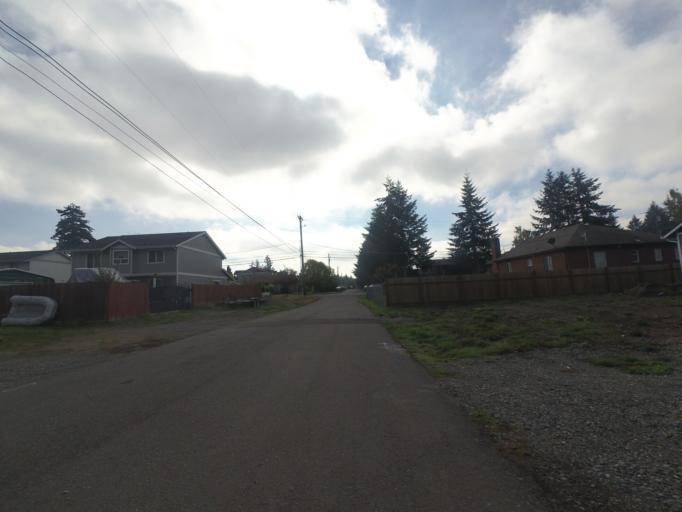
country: US
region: Washington
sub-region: Pierce County
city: Lakewood
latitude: 47.1998
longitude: -122.5072
